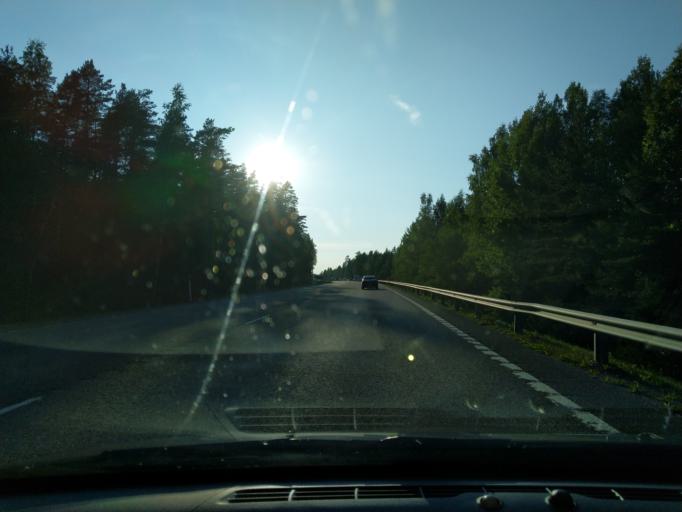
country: FI
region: Paijanne Tavastia
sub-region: Lahti
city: Lahti
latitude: 60.9652
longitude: 25.7440
